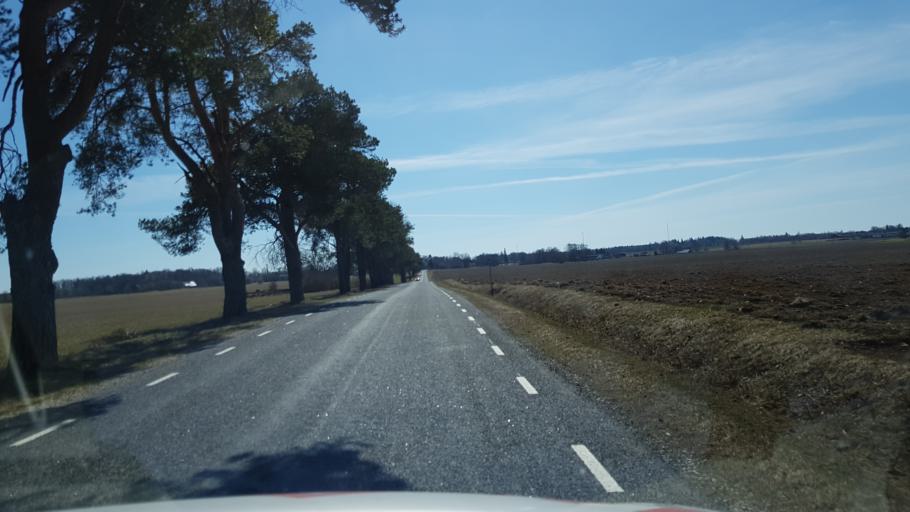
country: EE
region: Laeaene-Virumaa
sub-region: Vinni vald
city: Vinni
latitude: 59.1083
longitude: 26.5250
